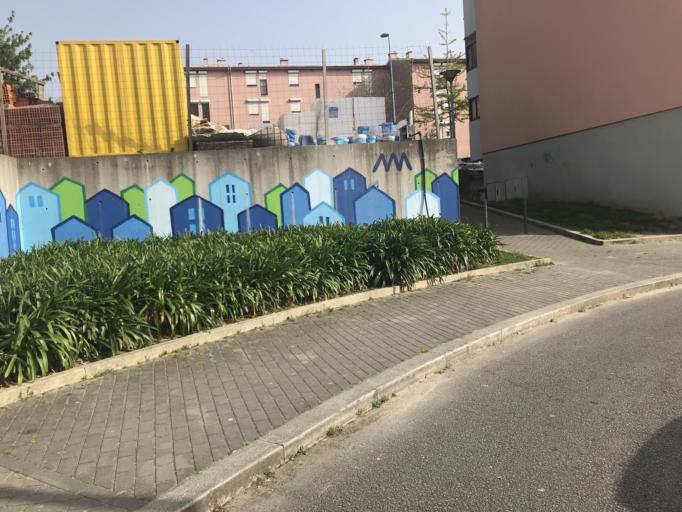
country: PT
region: Porto
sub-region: Matosinhos
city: Matosinhos
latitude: 41.1759
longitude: -8.6722
